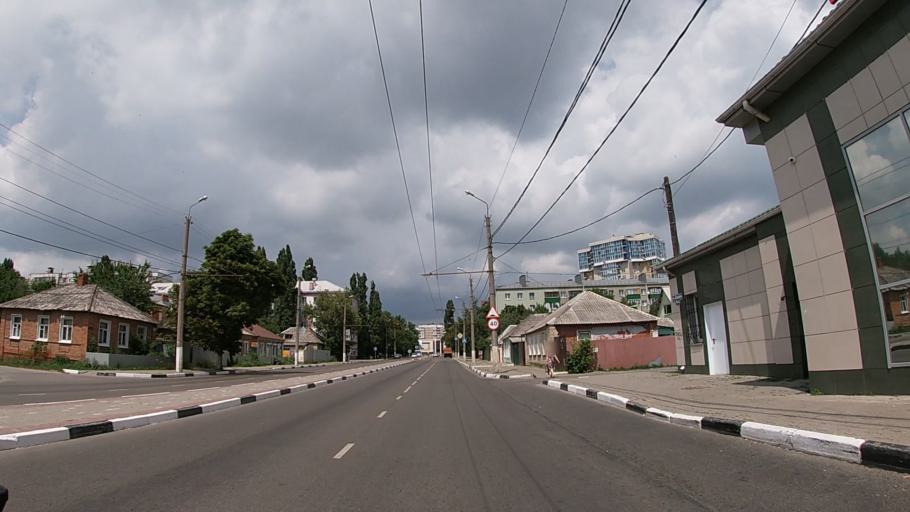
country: RU
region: Belgorod
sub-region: Belgorodskiy Rayon
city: Belgorod
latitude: 50.6103
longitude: 36.5918
